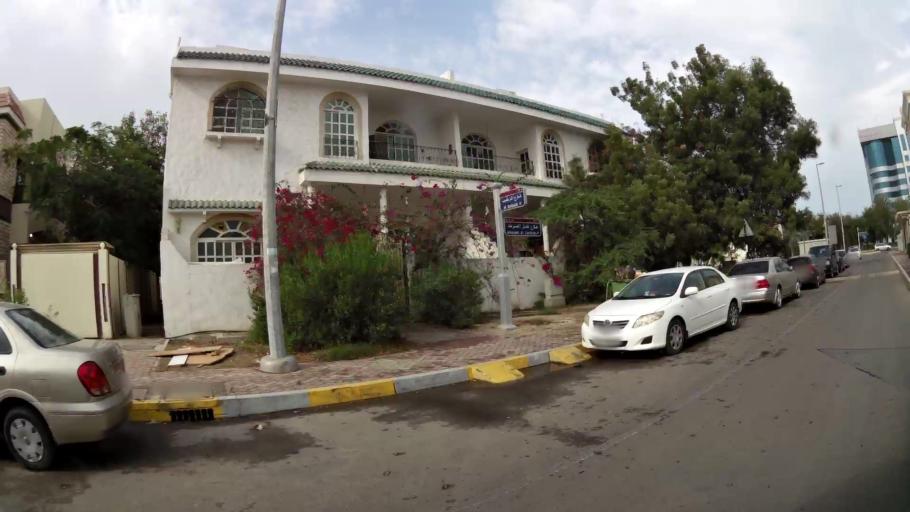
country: AE
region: Abu Dhabi
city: Abu Dhabi
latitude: 24.4505
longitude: 54.3988
